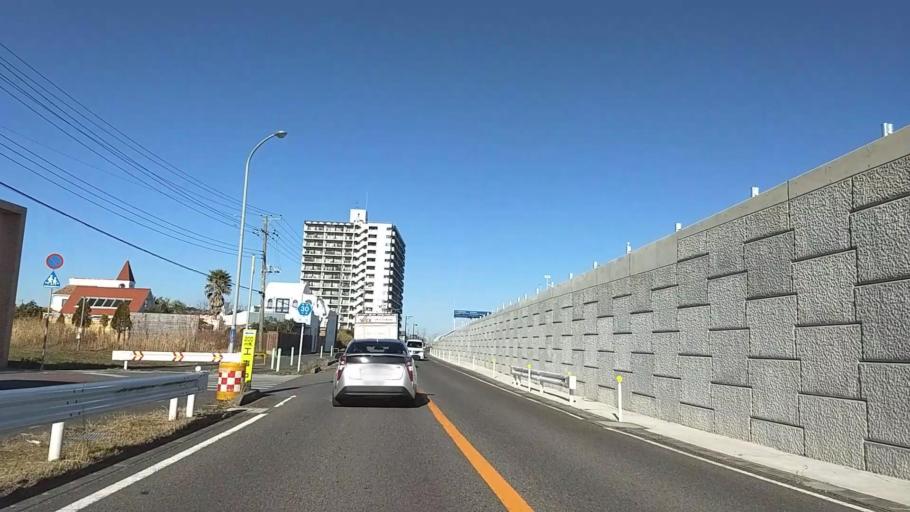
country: JP
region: Chiba
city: Togane
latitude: 35.4510
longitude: 140.4031
